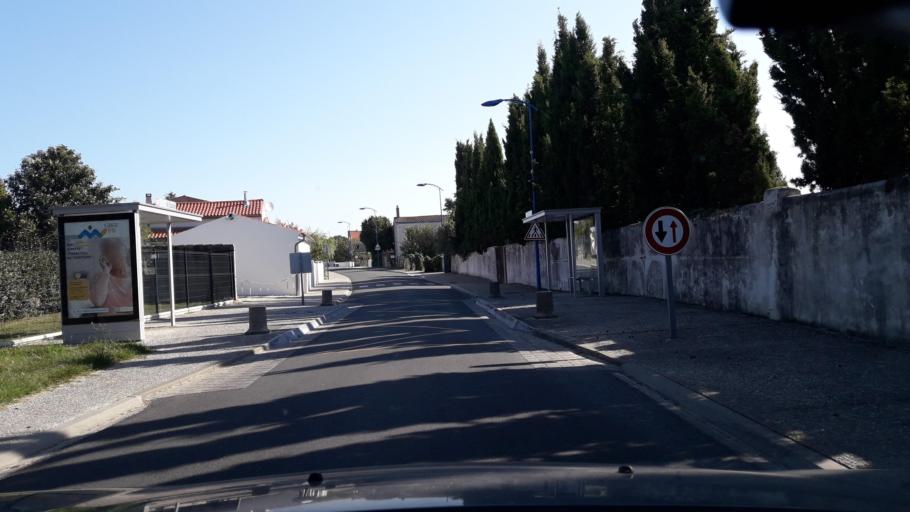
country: FR
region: Poitou-Charentes
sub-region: Departement de la Charente-Maritime
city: Etaules
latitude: 45.7158
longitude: -1.1079
